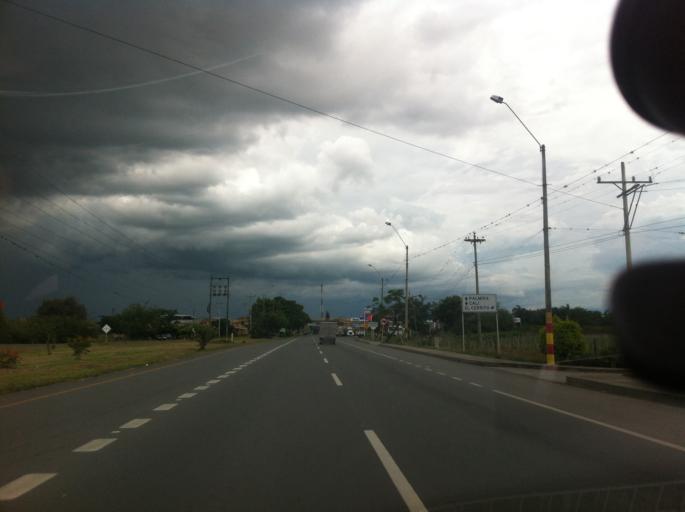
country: CO
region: Valle del Cauca
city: El Cerrito
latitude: 3.6973
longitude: -76.3164
